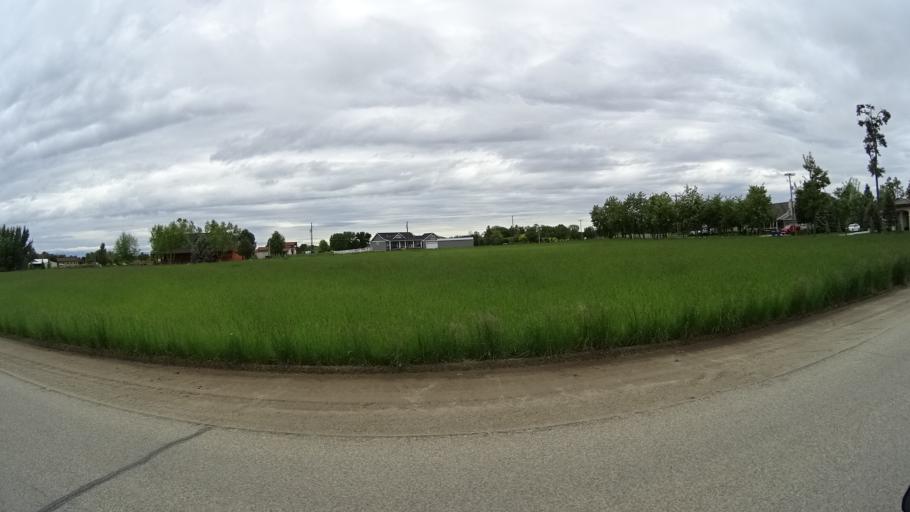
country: US
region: Idaho
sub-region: Ada County
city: Eagle
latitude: 43.7277
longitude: -116.3793
